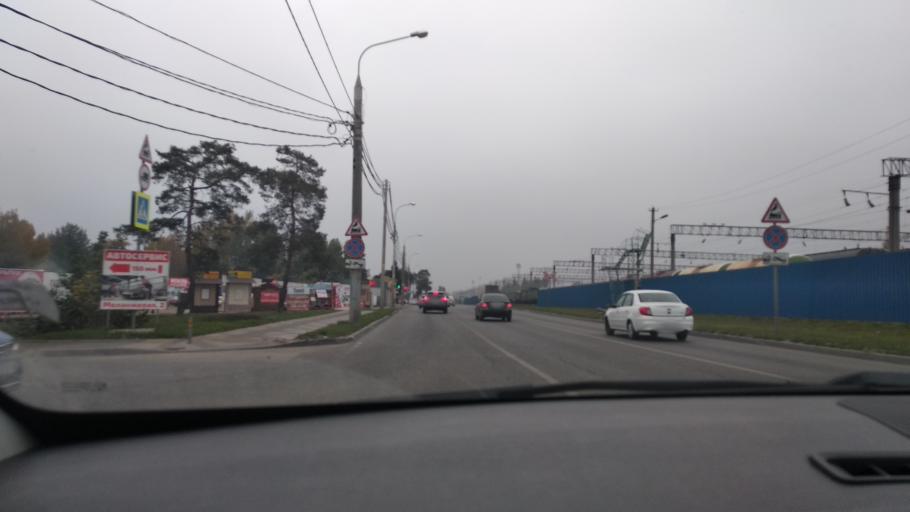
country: RU
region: Krasnodarskiy
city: Pashkovskiy
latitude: 45.0369
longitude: 39.0478
